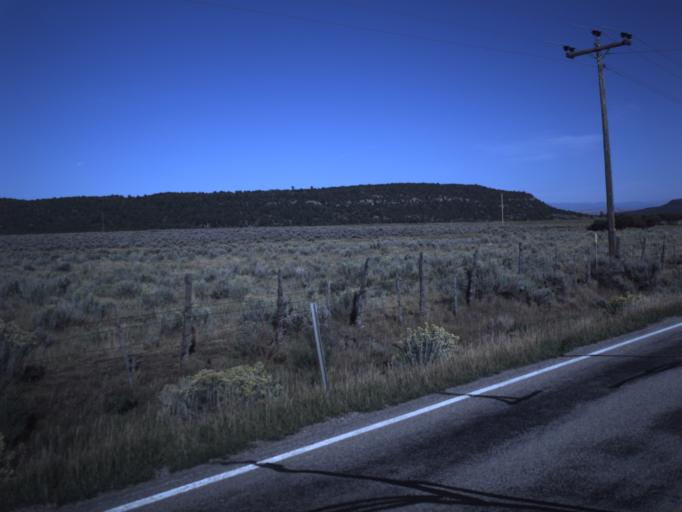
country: US
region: Utah
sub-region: Grand County
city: Moab
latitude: 38.3329
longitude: -109.1527
